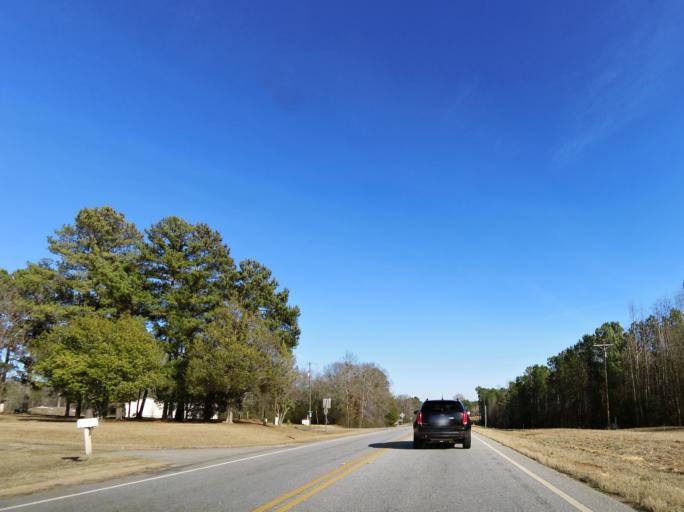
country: US
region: Georgia
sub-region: Crawford County
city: Roberta
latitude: 32.7525
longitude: -84.1752
